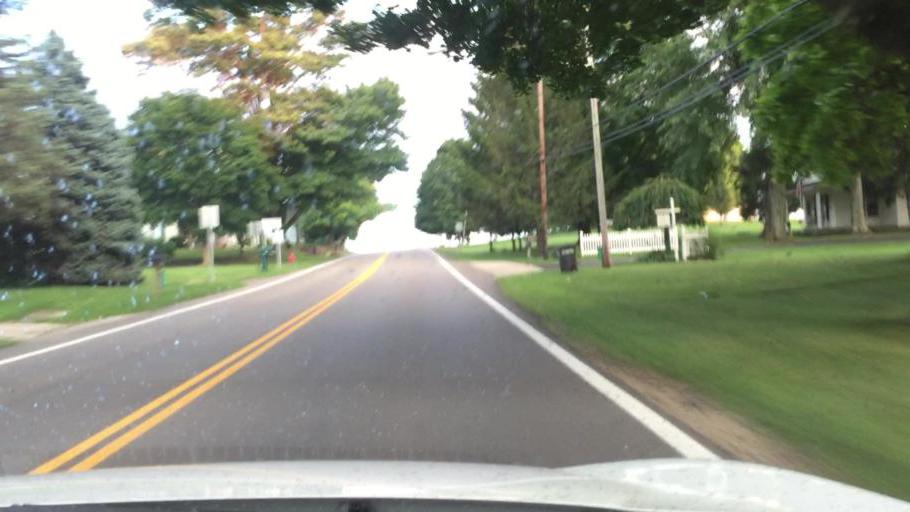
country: US
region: Ohio
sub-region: Champaign County
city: Mechanicsburg
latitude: 40.0669
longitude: -83.5501
